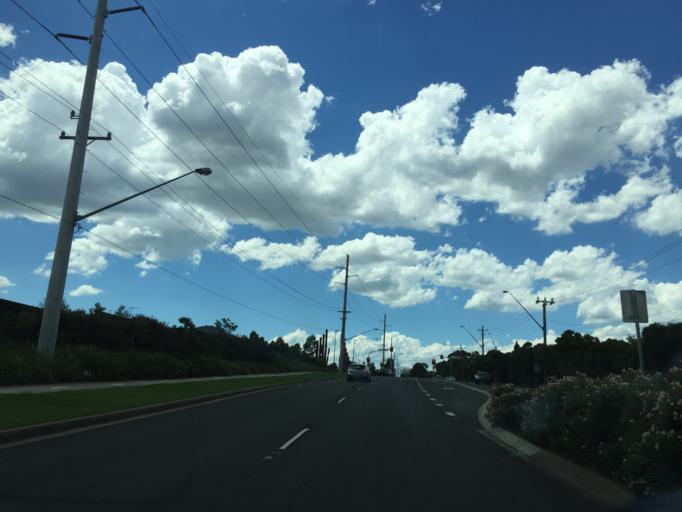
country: AU
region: New South Wales
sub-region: Blacktown
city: Doonside
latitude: -33.7814
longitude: 150.8729
